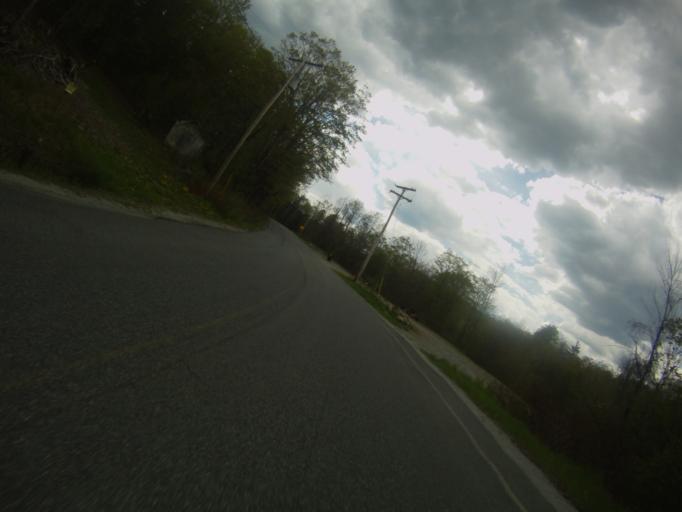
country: US
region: New York
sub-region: Essex County
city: Mineville
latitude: 44.0533
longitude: -73.5477
